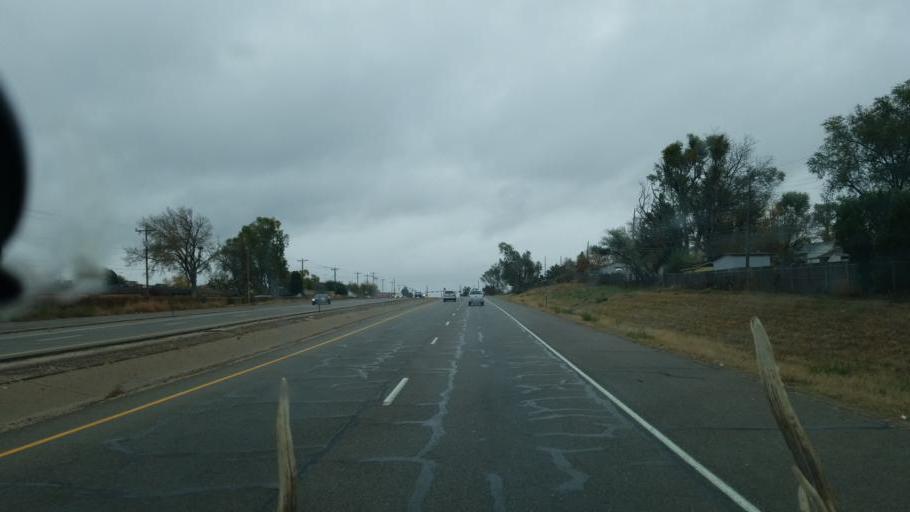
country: US
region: Colorado
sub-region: Pueblo County
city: Pueblo
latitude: 38.2860
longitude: -104.5926
